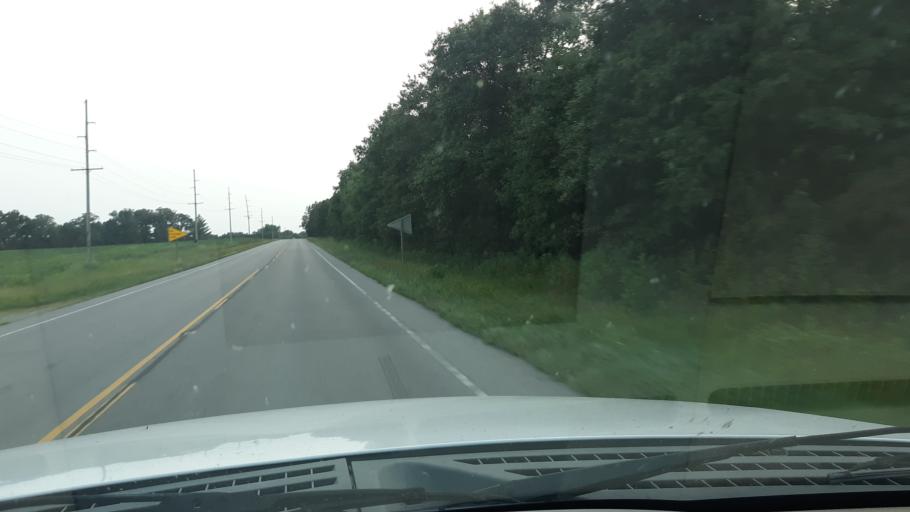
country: US
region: Illinois
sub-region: White County
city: Norris City
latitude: 38.0321
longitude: -88.2543
